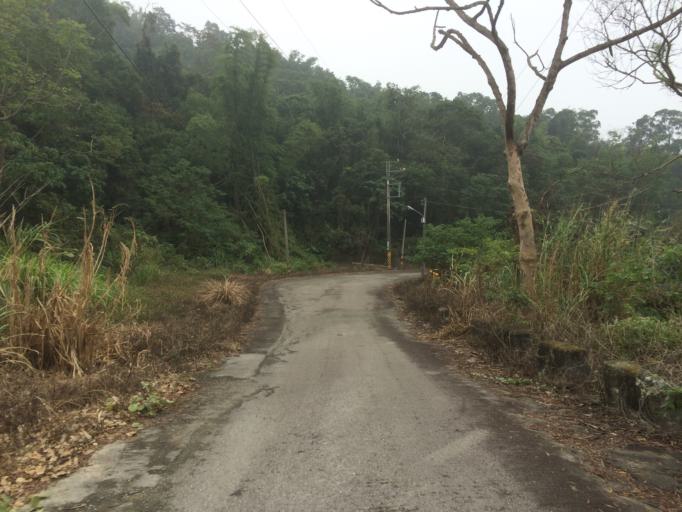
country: TW
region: Taiwan
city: Fengyuan
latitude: 24.1715
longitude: 120.7859
